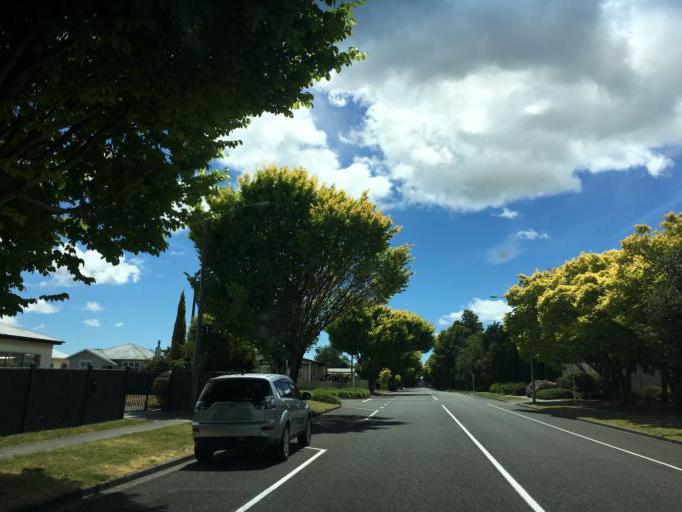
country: NZ
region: Hawke's Bay
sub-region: Hastings District
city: Hastings
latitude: -39.6450
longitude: 176.8584
